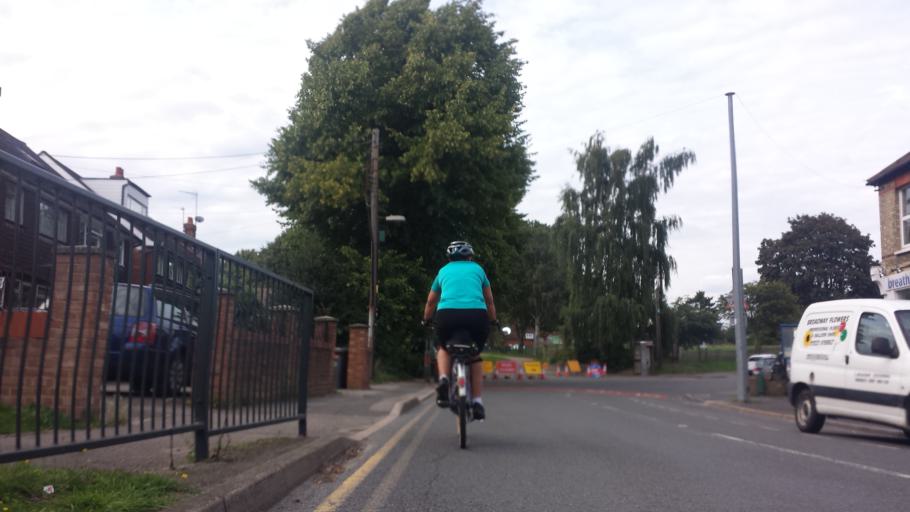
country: GB
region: England
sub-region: Kent
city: Swanley
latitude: 51.3835
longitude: 0.1610
